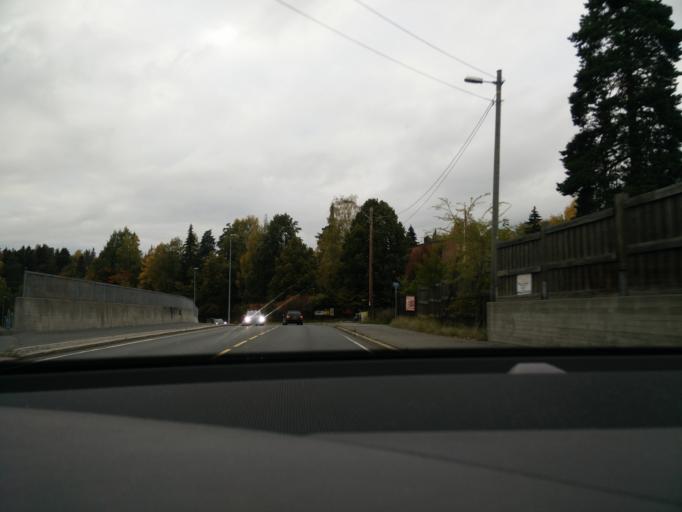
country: NO
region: Akershus
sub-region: Baerum
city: Lysaker
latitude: 59.9262
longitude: 10.6297
